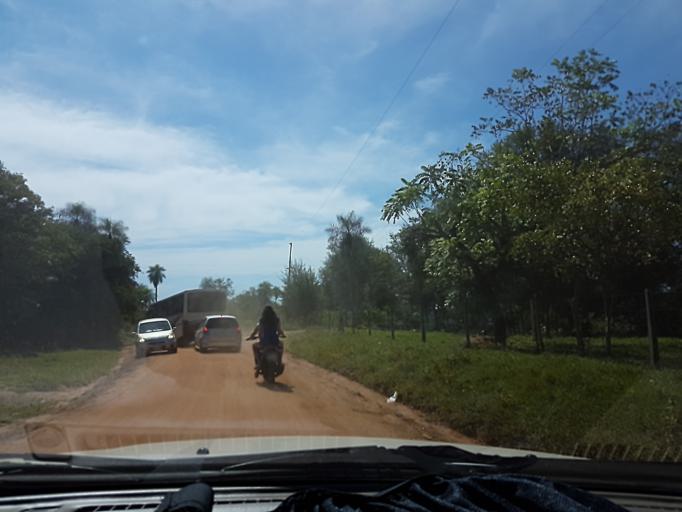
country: PY
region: Cordillera
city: Arroyos y Esteros
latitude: -24.9897
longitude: -57.2118
